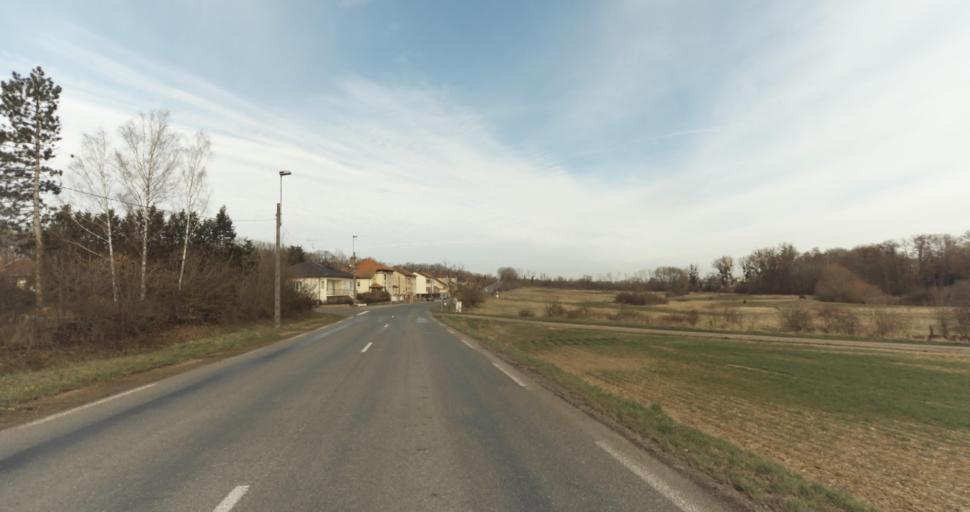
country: FR
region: Lorraine
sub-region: Departement de Meurthe-et-Moselle
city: Jarny
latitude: 49.1436
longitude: 5.8874
